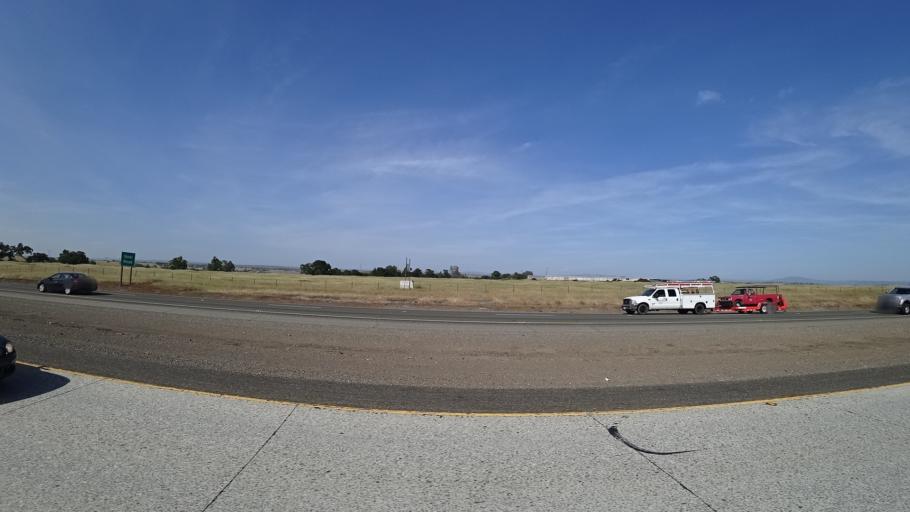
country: US
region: California
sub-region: Butte County
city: Durham
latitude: 39.6630
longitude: -121.7404
